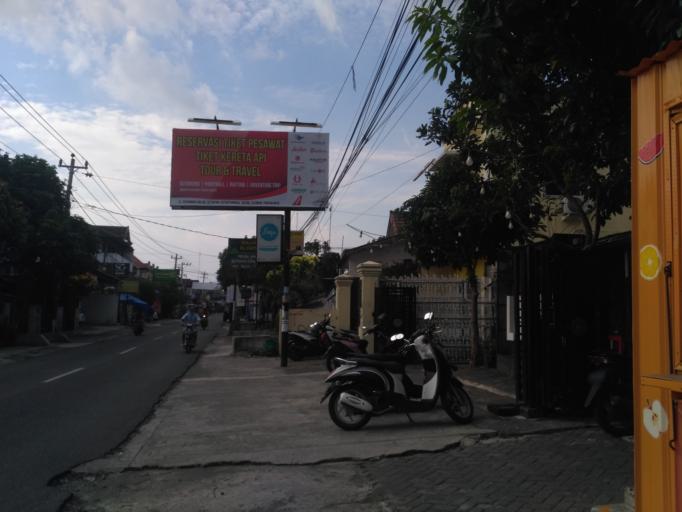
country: ID
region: Daerah Istimewa Yogyakarta
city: Depok
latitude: -7.7669
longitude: 110.4057
